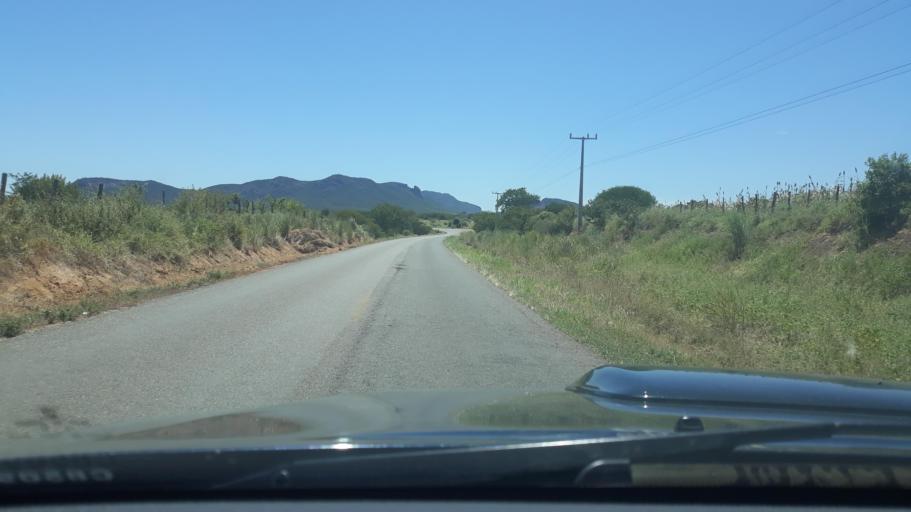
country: BR
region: Bahia
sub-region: Guanambi
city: Guanambi
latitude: -14.1731
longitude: -42.8029
